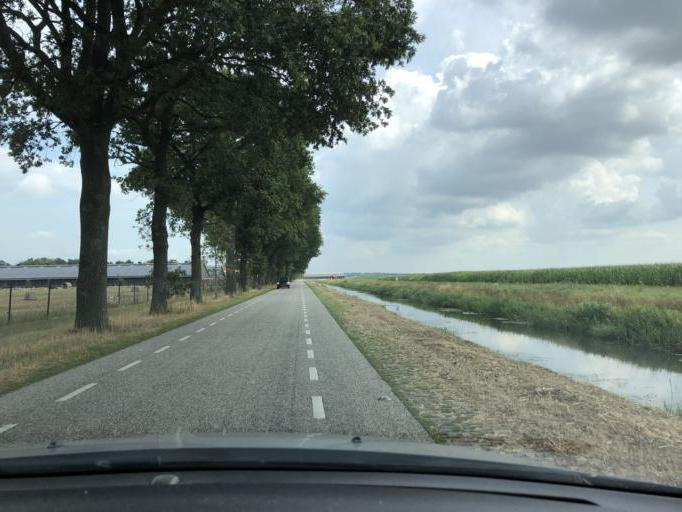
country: NL
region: Drenthe
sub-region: Gemeente Coevorden
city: Dalen
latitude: 52.7903
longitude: 6.6360
